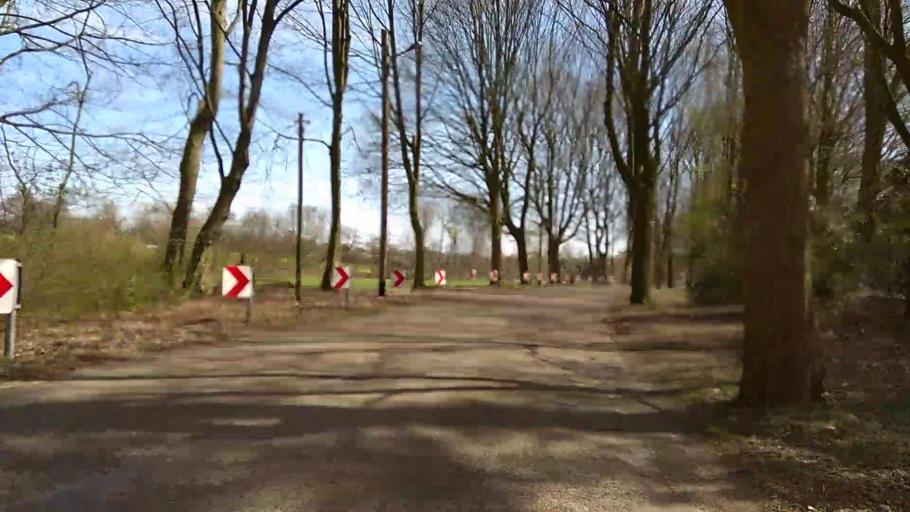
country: DE
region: North Rhine-Westphalia
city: Herten
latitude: 51.5772
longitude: 7.0854
